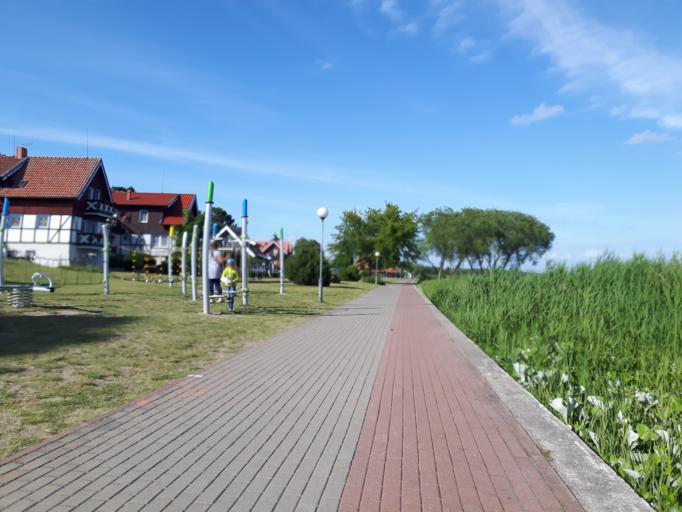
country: LT
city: Nida
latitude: 55.3148
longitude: 21.0165
